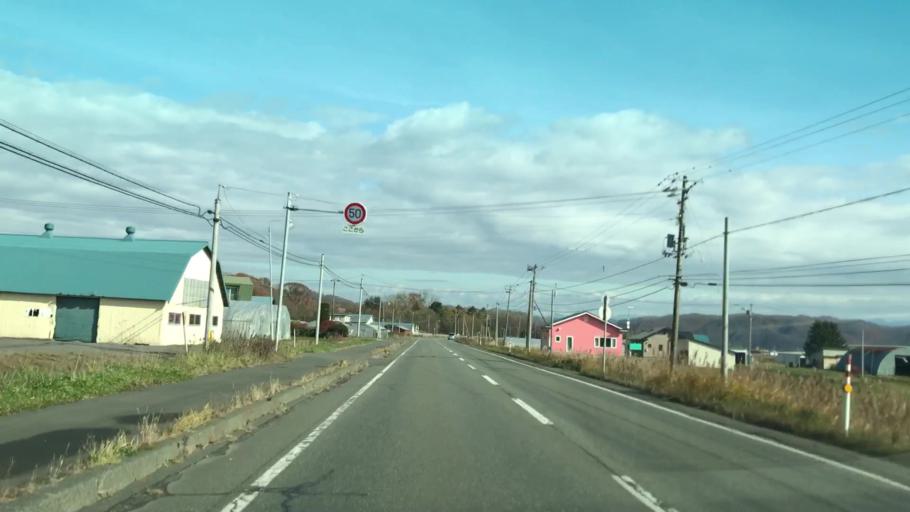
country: JP
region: Hokkaido
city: Shizunai-furukawacho
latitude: 42.5741
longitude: 142.1051
